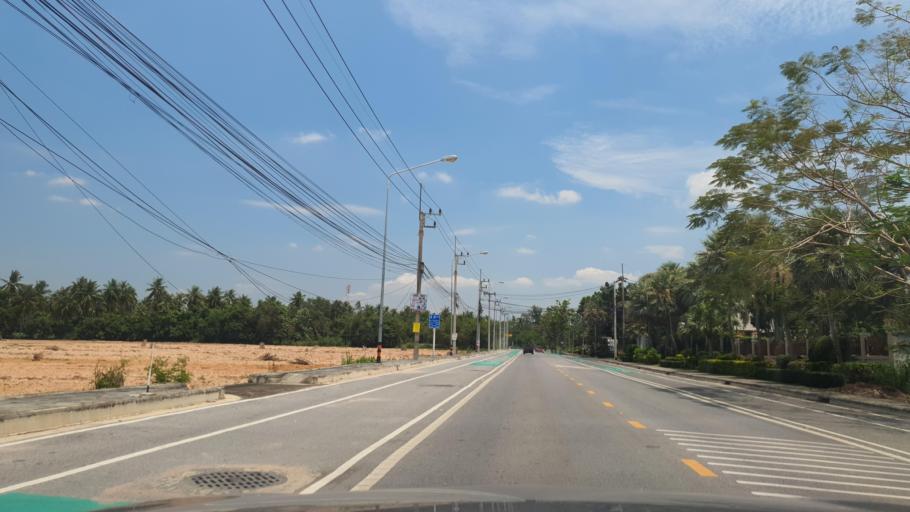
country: TH
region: Rayong
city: Ban Chang
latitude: 12.7984
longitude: 100.9472
